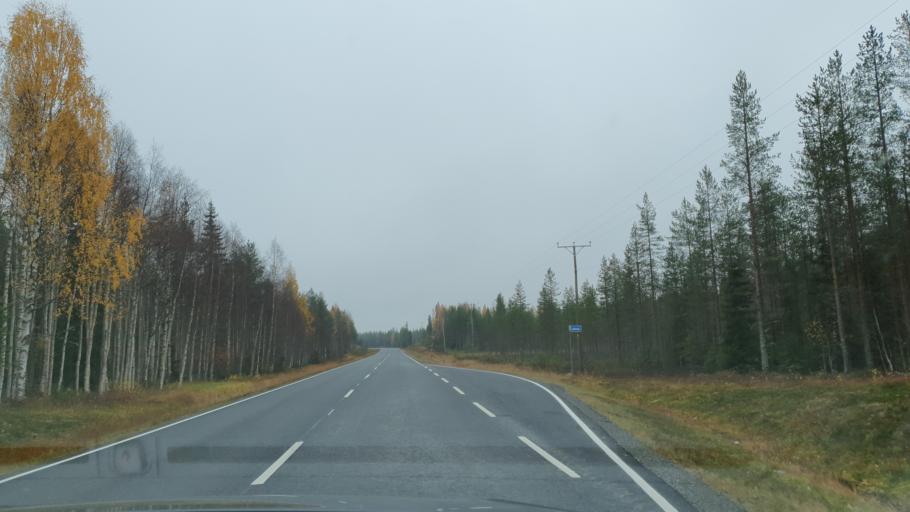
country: FI
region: Lapland
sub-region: Rovaniemi
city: Ranua
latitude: 66.1378
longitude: 26.2740
